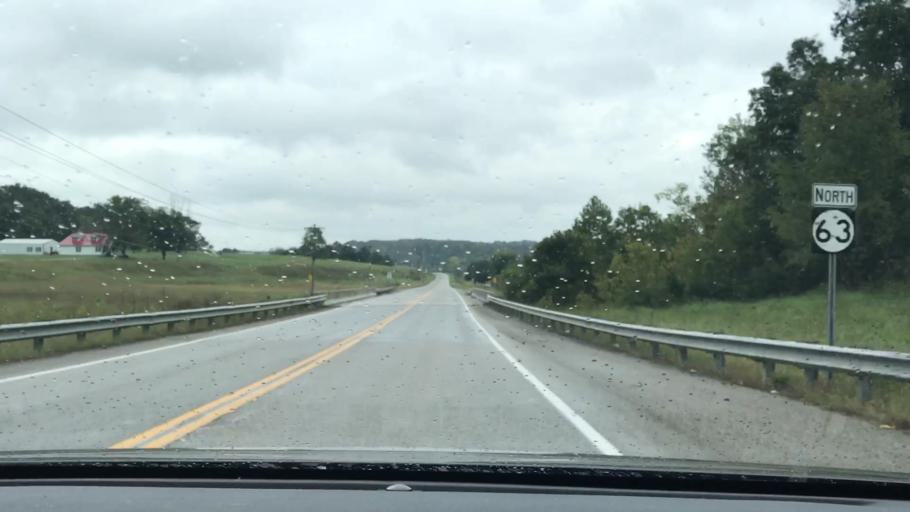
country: US
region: Kentucky
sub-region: Monroe County
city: Tompkinsville
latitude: 36.6724
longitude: -85.7271
